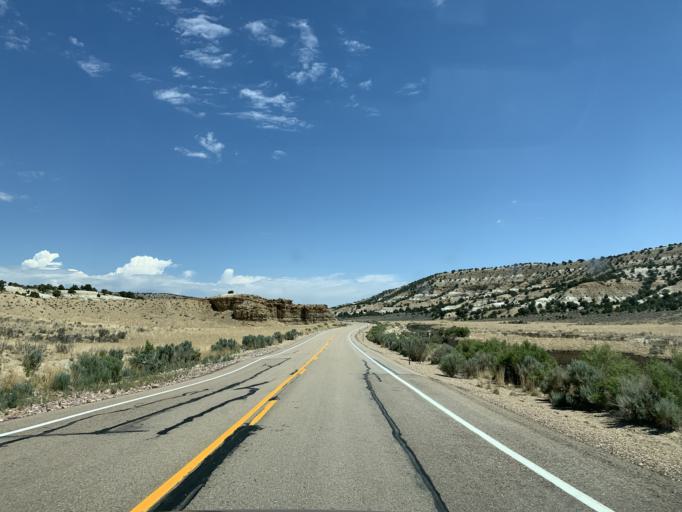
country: US
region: Utah
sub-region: Duchesne County
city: Duchesne
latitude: 39.9521
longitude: -110.1946
